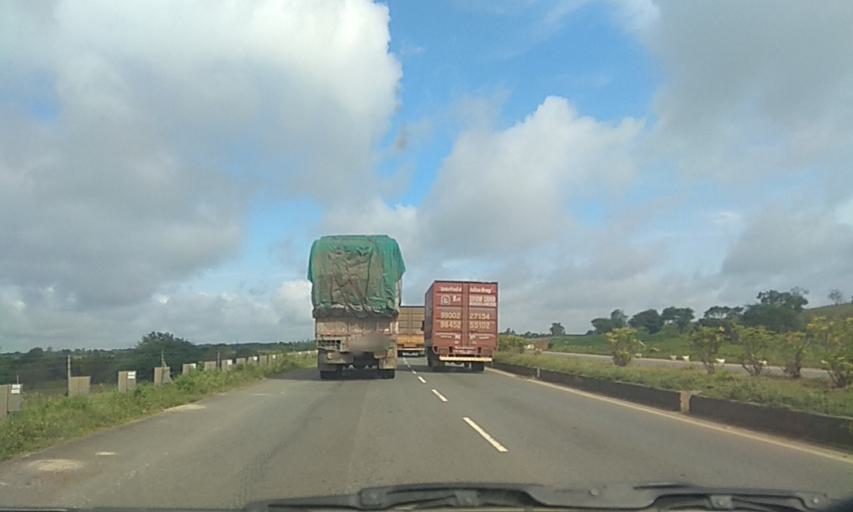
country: IN
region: Karnataka
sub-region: Haveri
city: Shiggaon
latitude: 15.0181
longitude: 75.1853
